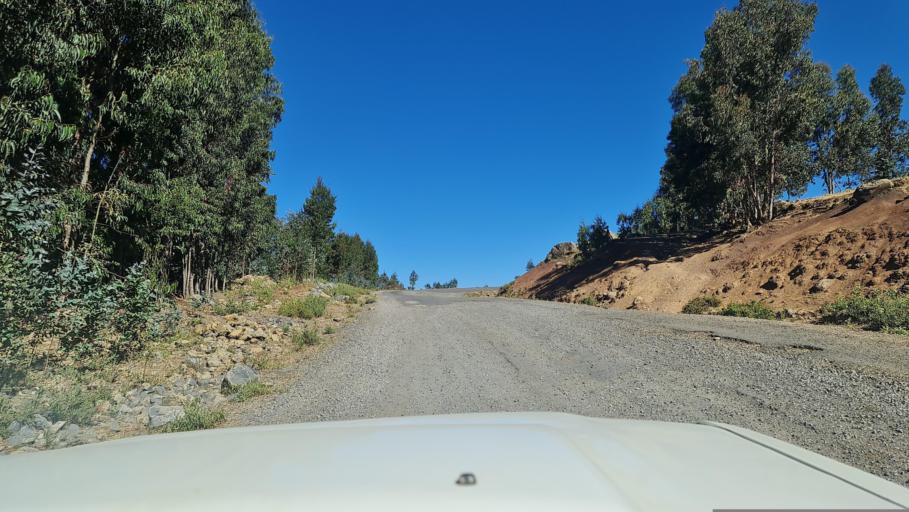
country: ET
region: Amhara
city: Debark'
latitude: 13.1107
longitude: 38.1491
